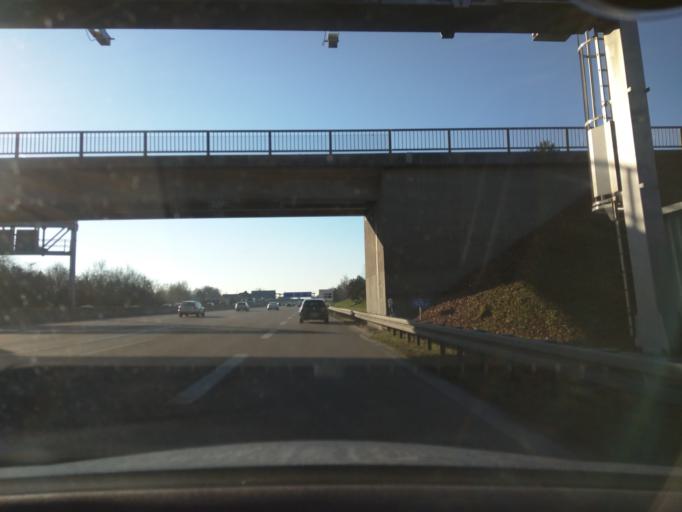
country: DE
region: Bavaria
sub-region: Upper Bavaria
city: Unterfoehring
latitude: 48.2115
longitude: 11.6242
